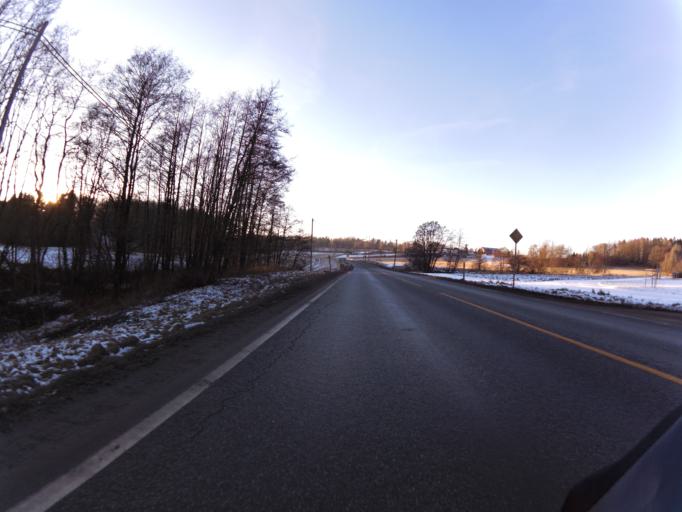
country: NO
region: Ostfold
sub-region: Fredrikstad
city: Fredrikstad
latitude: 59.2535
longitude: 10.8628
